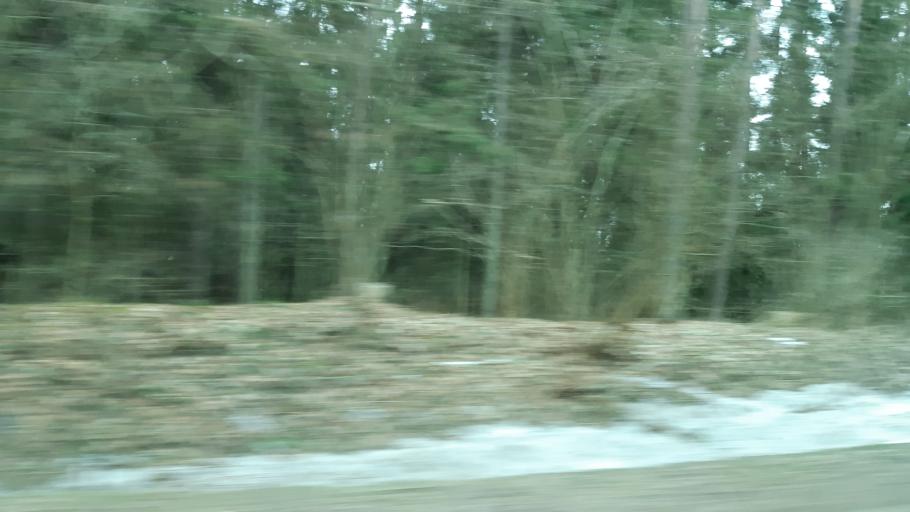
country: PL
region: Podlasie
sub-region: Suwalki
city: Suwalki
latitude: 54.2781
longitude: 22.9395
